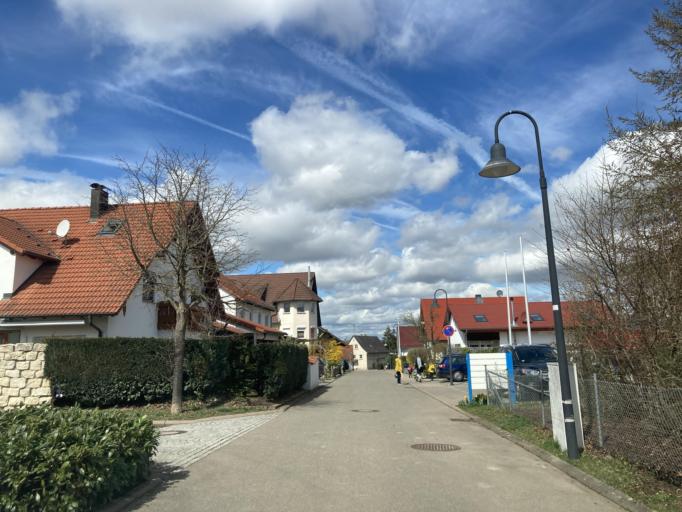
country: DE
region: Baden-Wuerttemberg
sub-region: Regierungsbezirk Stuttgart
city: Bondorf
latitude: 48.4707
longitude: 8.8181
